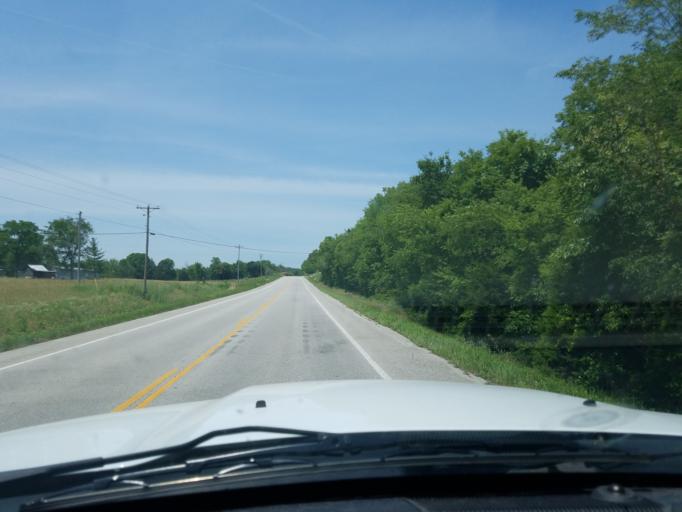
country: US
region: Tennessee
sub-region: Trousdale County
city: Hartsville
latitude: 36.4086
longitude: -86.2670
